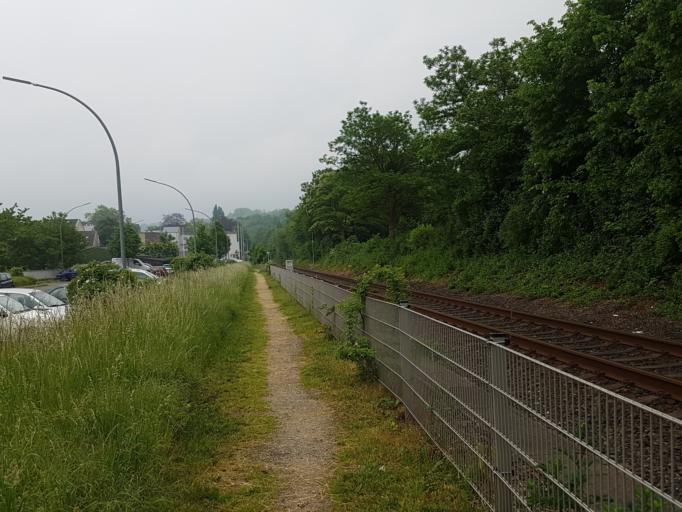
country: DE
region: North Rhine-Westphalia
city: Stolberg
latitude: 50.7754
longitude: 6.2225
